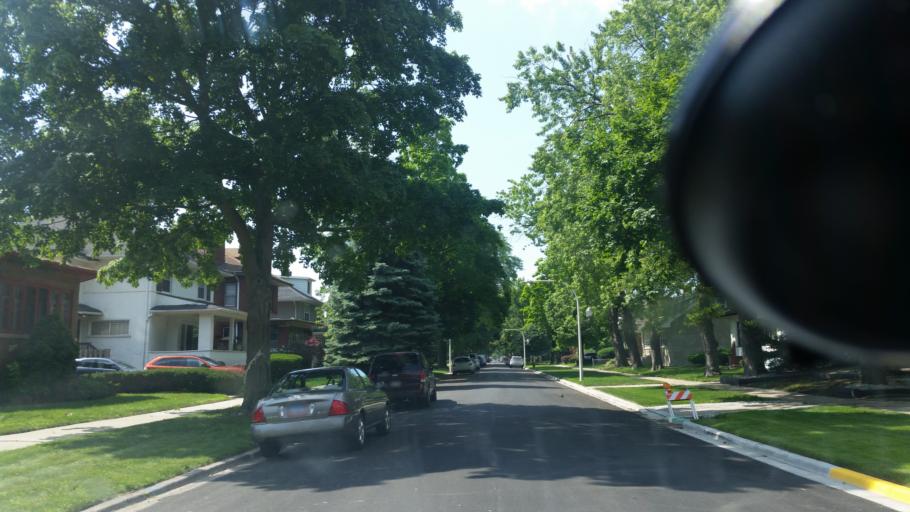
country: US
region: Indiana
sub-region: Lake County
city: Whiting
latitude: 41.7644
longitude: -87.5689
